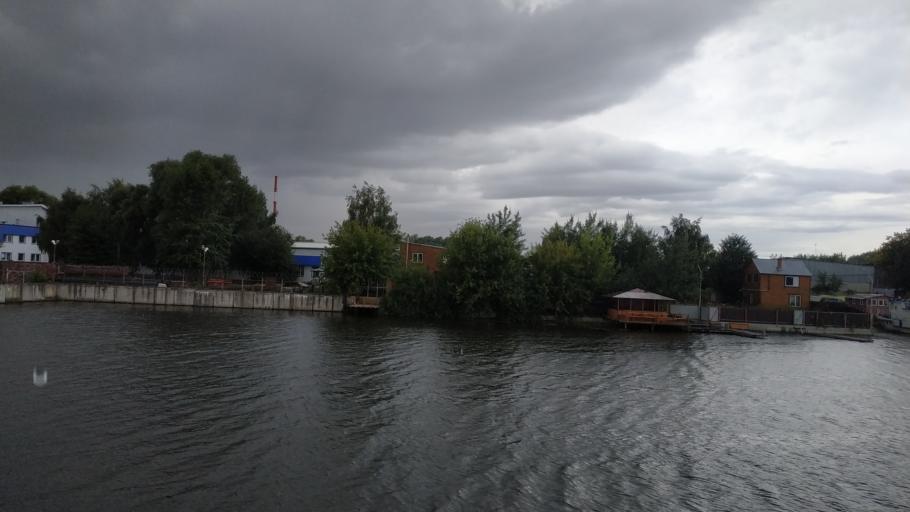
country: RU
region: Moskovskaya
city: Alekseyevka
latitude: 55.6169
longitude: 37.7973
